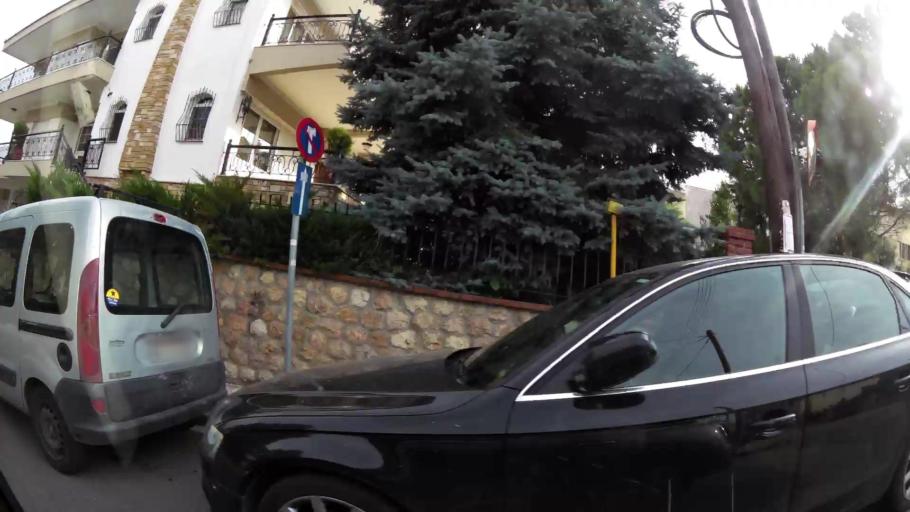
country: GR
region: Central Macedonia
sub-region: Nomos Thessalonikis
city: Oraiokastro
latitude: 40.7306
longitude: 22.9158
